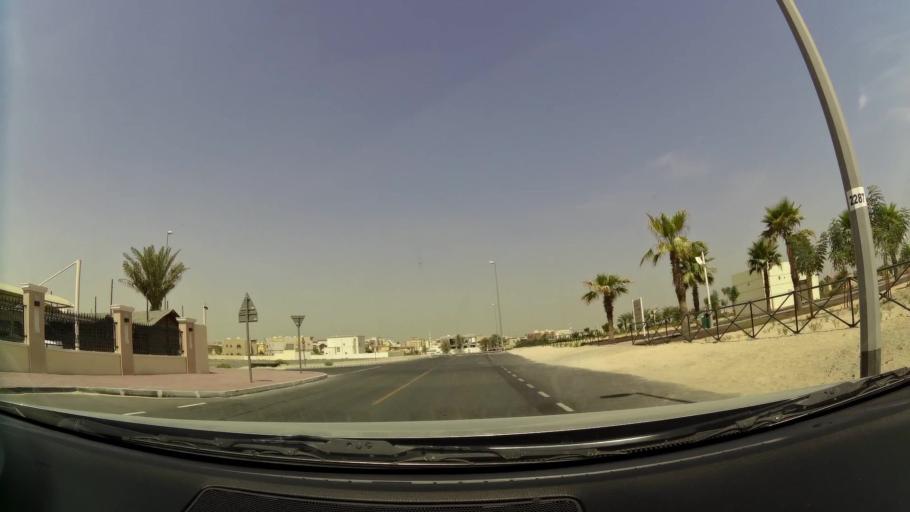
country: AE
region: Ash Shariqah
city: Sharjah
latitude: 25.1878
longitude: 55.4167
